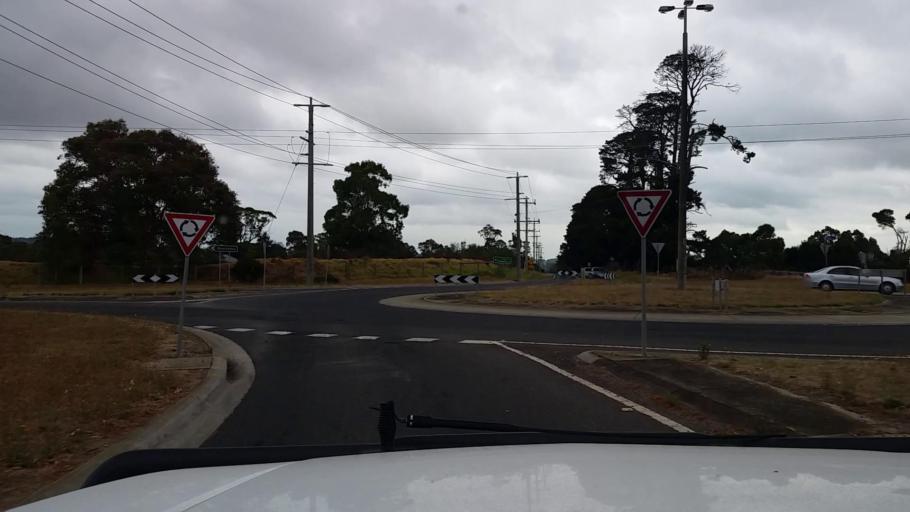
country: AU
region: Victoria
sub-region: Mornington Peninsula
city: Somerville
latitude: -38.2210
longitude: 145.1547
